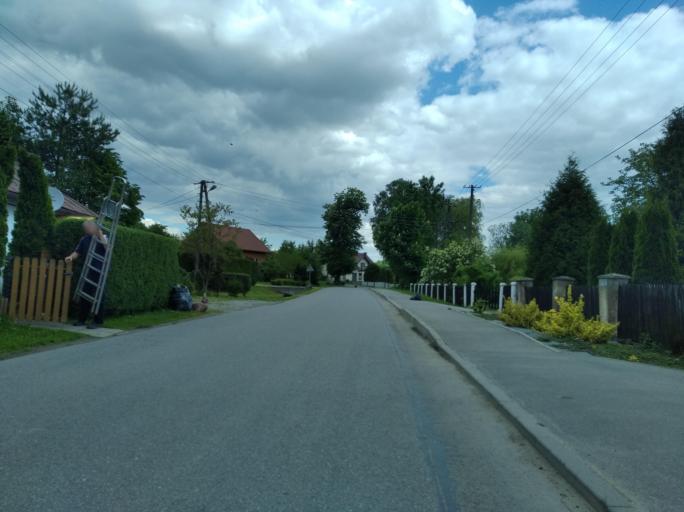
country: PL
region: Subcarpathian Voivodeship
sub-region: Powiat brzozowski
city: Jasionow
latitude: 49.6594
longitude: 21.9838
